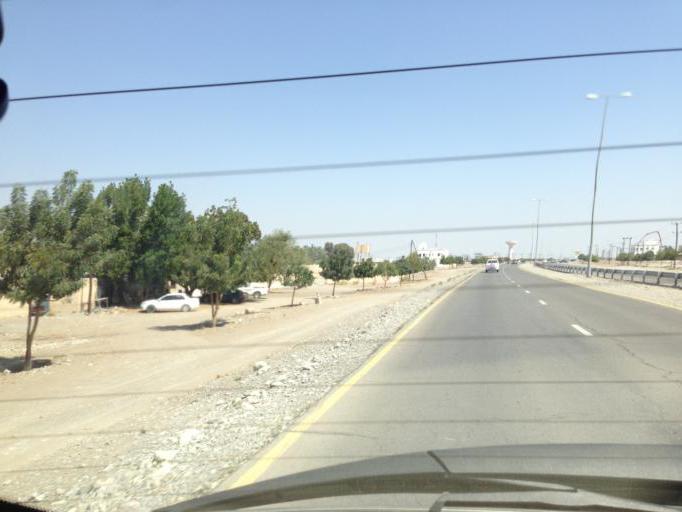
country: OM
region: Al Batinah
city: Rustaq
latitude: 23.5361
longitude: 57.4693
